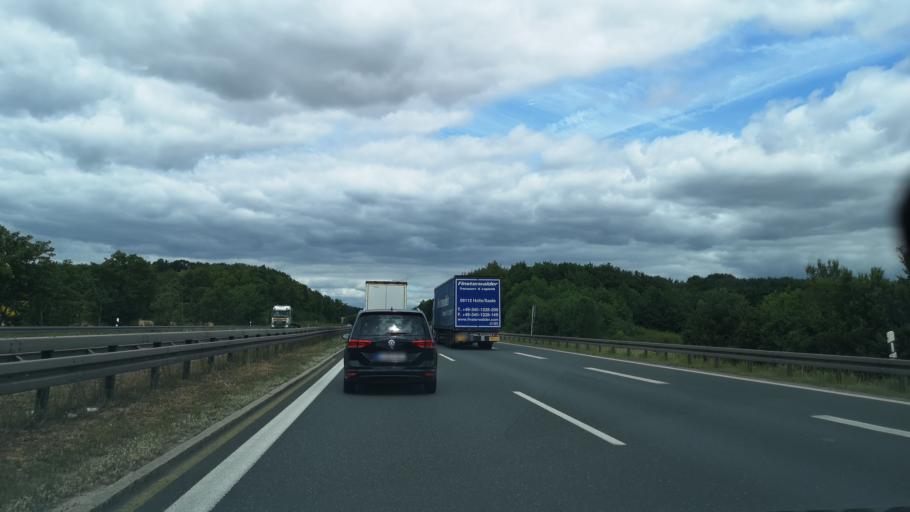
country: DE
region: Bavaria
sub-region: Regierungsbezirk Unterfranken
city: Wasserlosen
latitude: 50.0463
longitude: 10.0615
